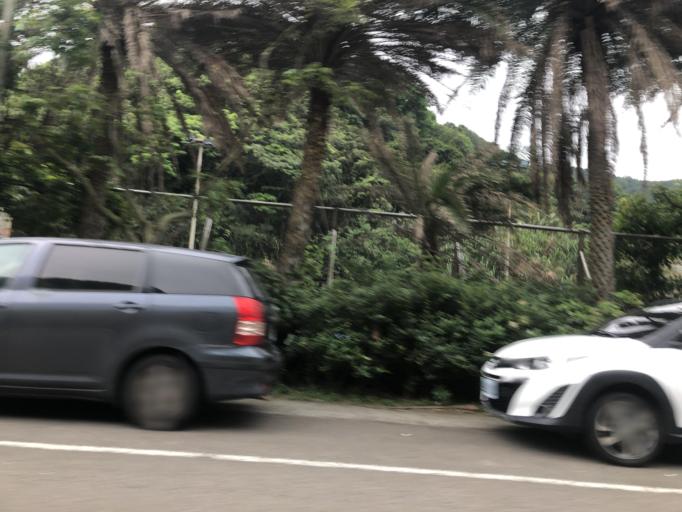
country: TW
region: Taiwan
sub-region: Keelung
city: Keelung
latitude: 25.2024
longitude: 121.6850
